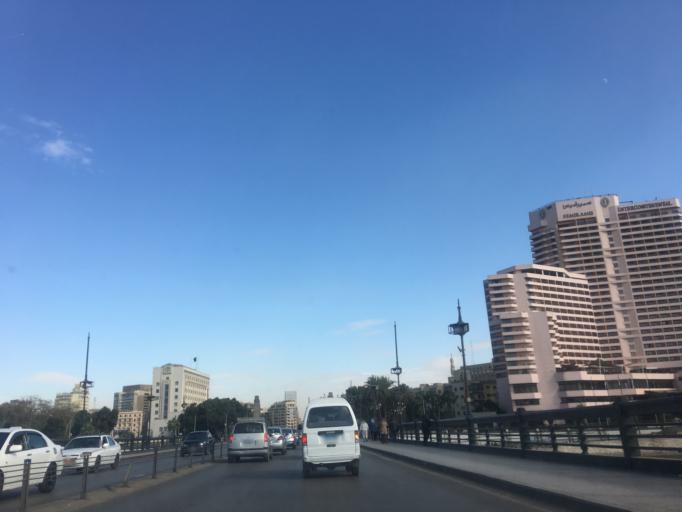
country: EG
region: Muhafazat al Qahirah
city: Cairo
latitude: 30.0437
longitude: 31.2297
